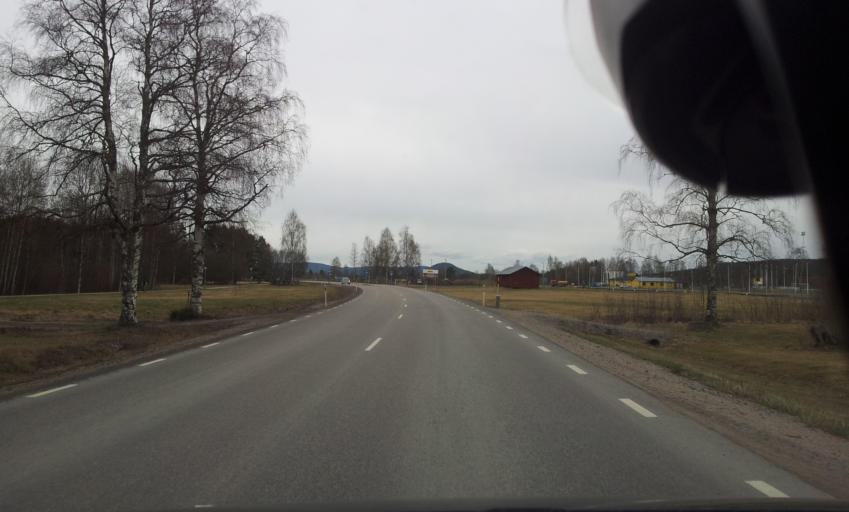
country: SE
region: Gaevleborg
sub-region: Ljusdals Kommun
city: Ljusdal
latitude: 61.8215
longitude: 16.0801
